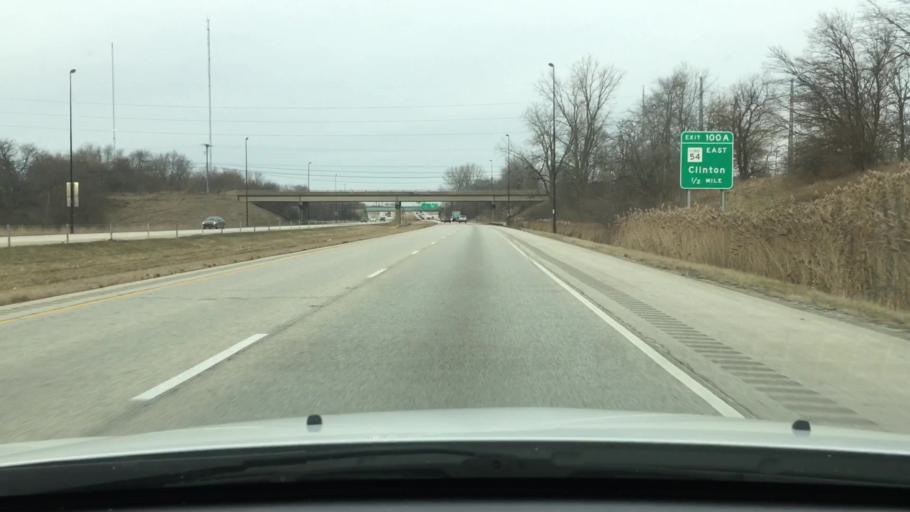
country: US
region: Illinois
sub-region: Sangamon County
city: Grandview
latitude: 39.8224
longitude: -89.5925
